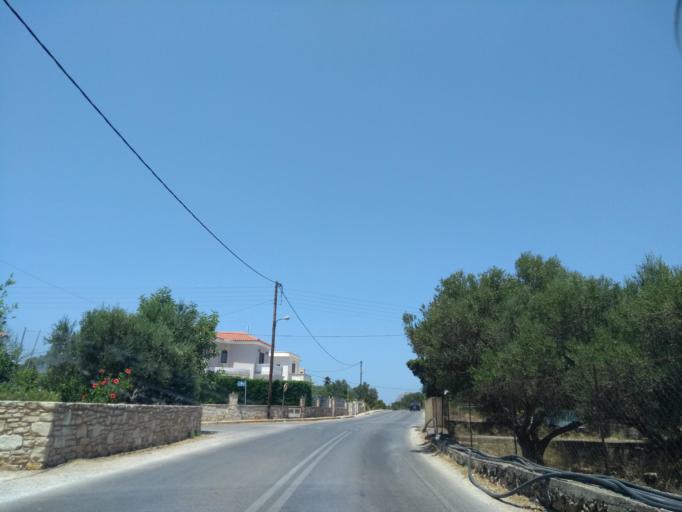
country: GR
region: Crete
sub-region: Nomos Chanias
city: Pithari
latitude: 35.5383
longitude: 24.0815
